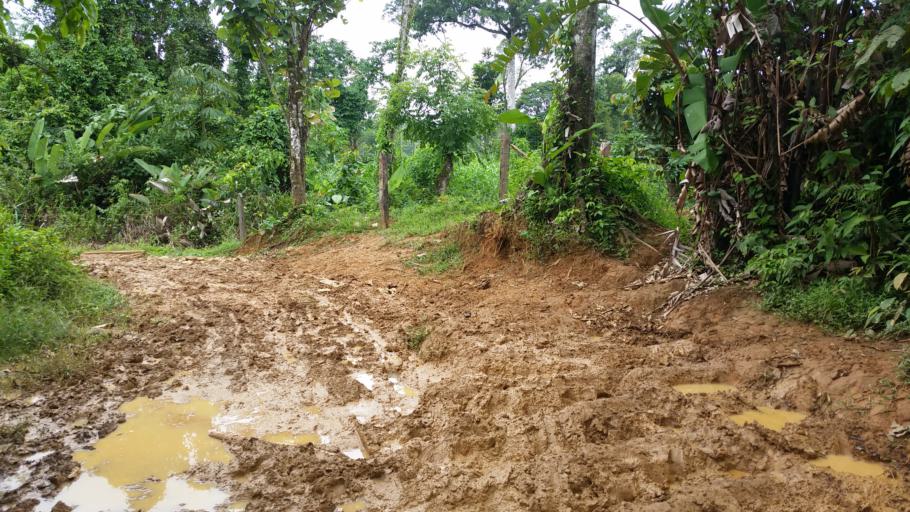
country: NI
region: Atlantico Norte (RAAN)
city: Bonanza
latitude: 13.9725
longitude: -84.7359
